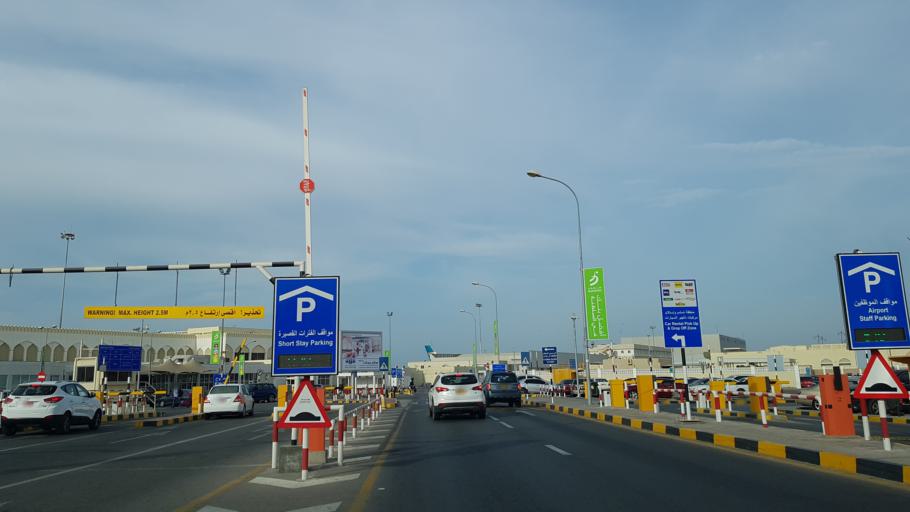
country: OM
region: Muhafazat Masqat
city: Bawshar
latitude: 23.5874
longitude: 58.2911
